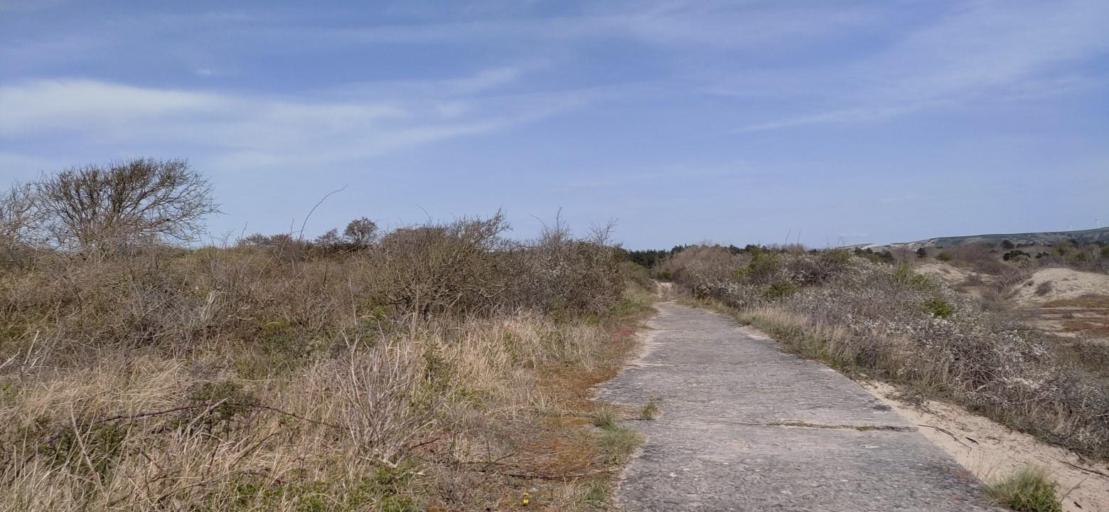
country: FR
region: Nord-Pas-de-Calais
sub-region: Departement du Pas-de-Calais
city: Camiers
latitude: 50.5585
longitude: 1.5917
